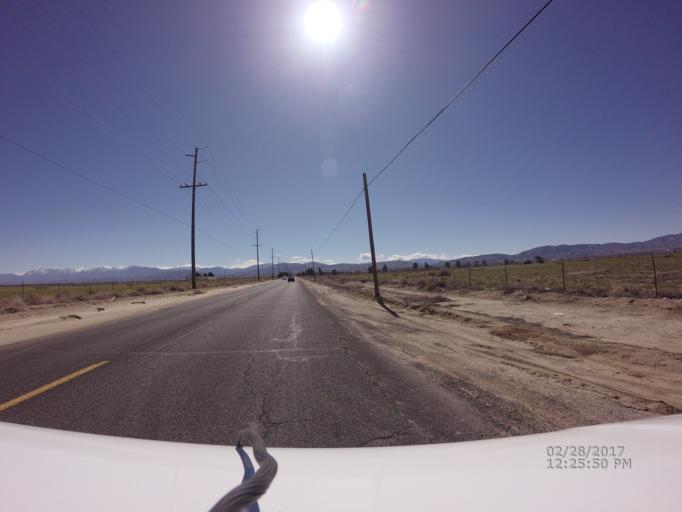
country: US
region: California
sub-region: Los Angeles County
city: Palmdale
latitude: 34.5982
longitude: -118.0584
